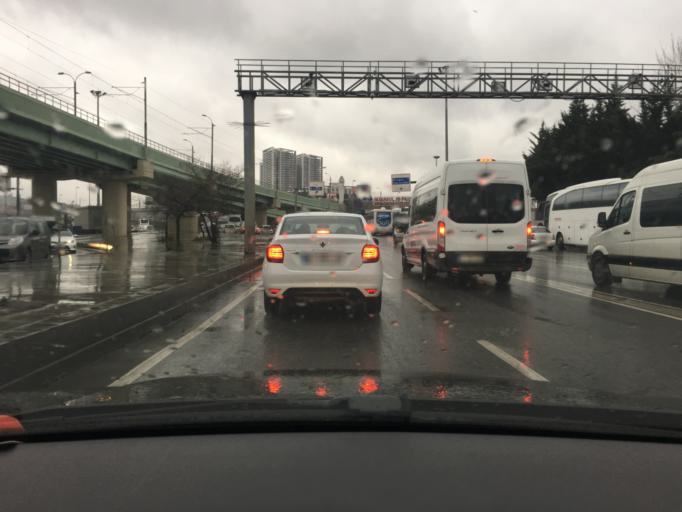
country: TR
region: Istanbul
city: Esenler
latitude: 41.0353
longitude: 28.8953
